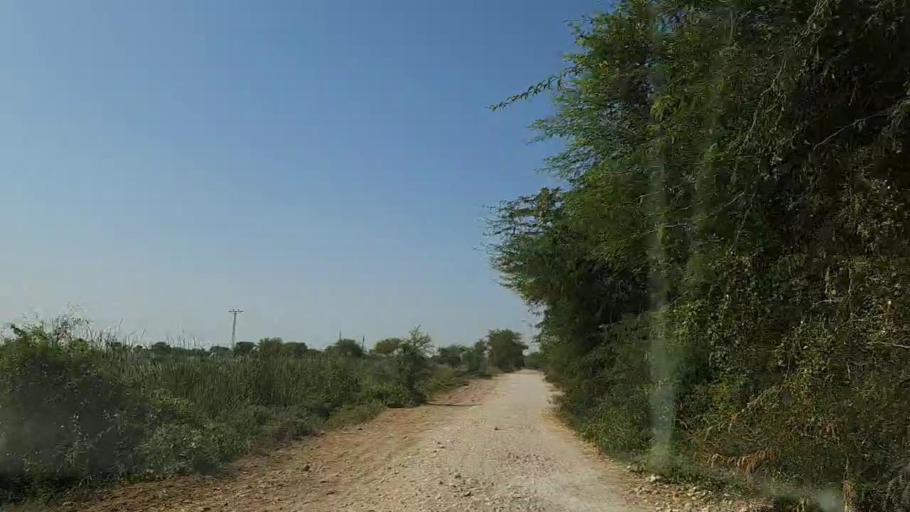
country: PK
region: Sindh
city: Chuhar Jamali
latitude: 24.4166
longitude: 68.0308
